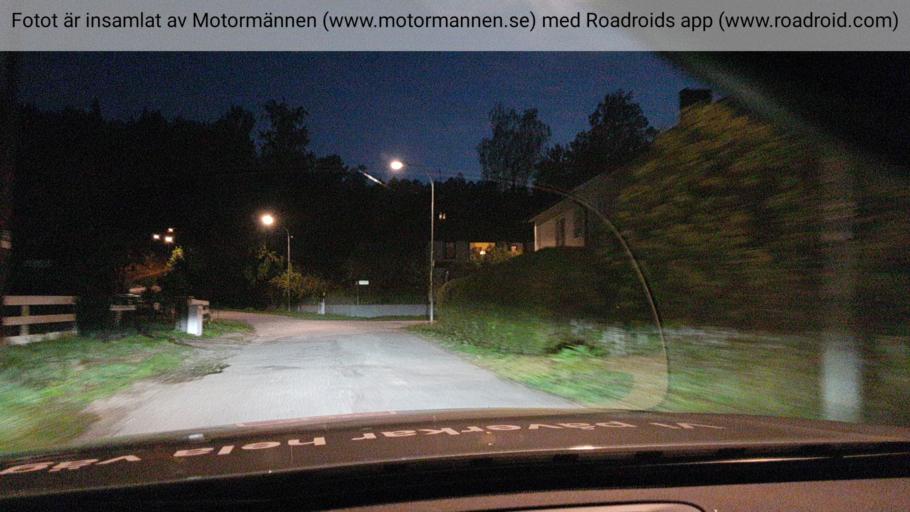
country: SE
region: Stockholm
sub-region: Huddinge Kommun
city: Huddinge
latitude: 59.2292
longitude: 17.9800
